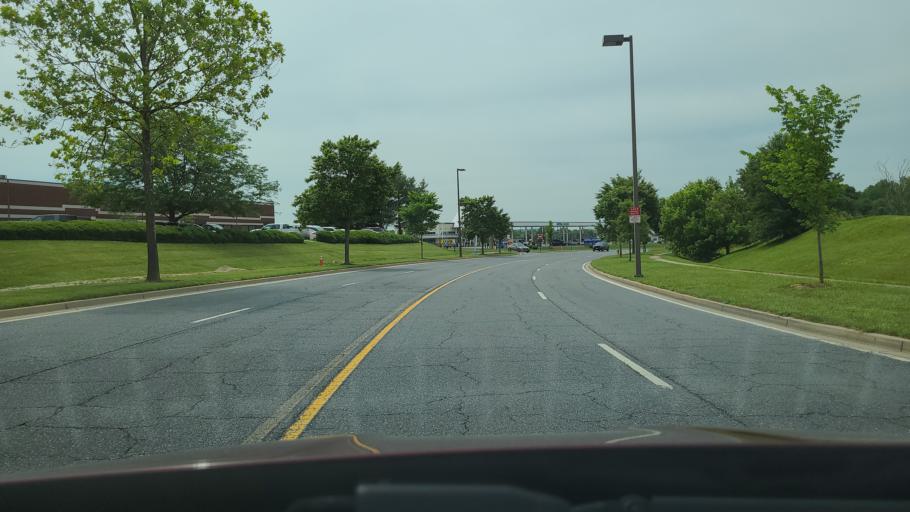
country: US
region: Maryland
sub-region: Frederick County
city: Frederick
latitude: 39.4371
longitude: -77.3767
